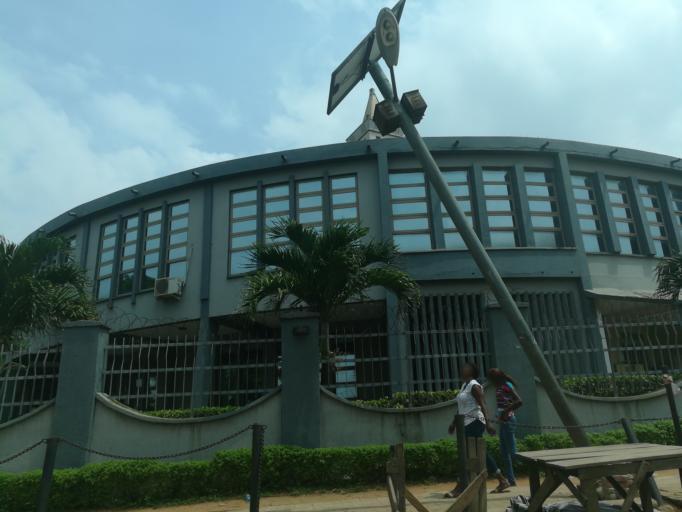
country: NG
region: Lagos
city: Ikorodu
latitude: 6.6128
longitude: 3.5048
